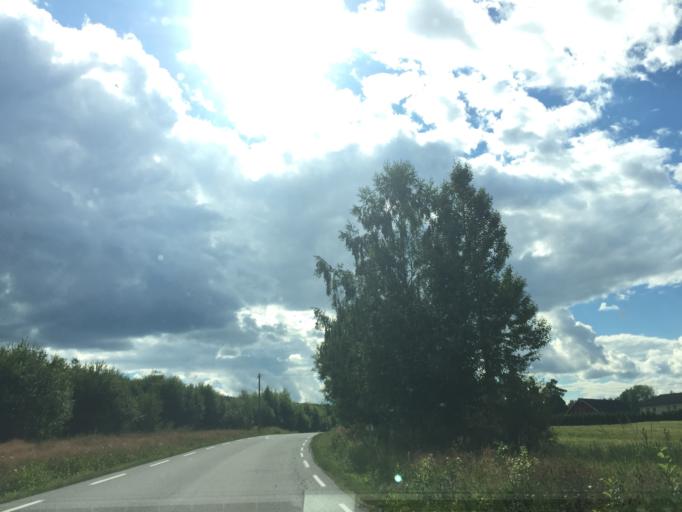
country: NO
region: Hedmark
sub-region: Kongsvinger
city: Spetalen
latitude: 60.1926
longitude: 11.8676
